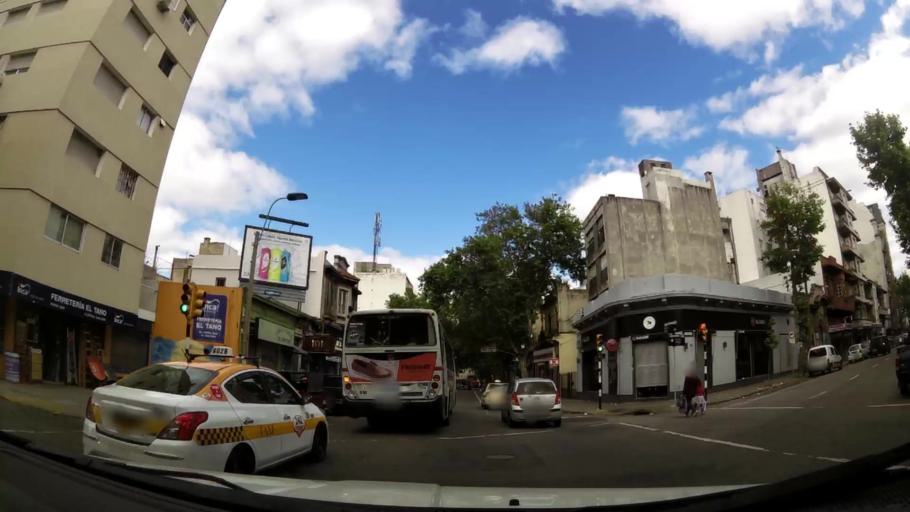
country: UY
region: Montevideo
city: Montevideo
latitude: -34.9023
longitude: -56.1718
